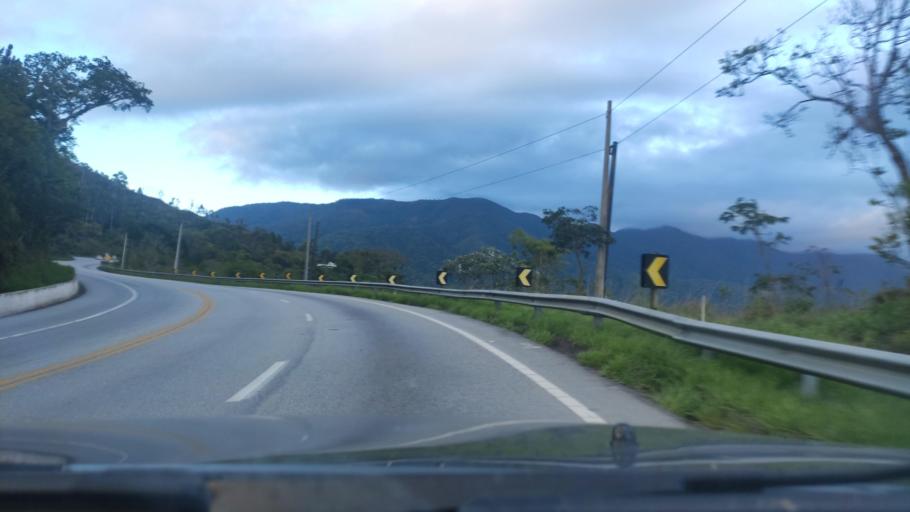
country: BR
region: Sao Paulo
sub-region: Campos Do Jordao
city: Campos do Jordao
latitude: -22.8492
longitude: -45.6137
